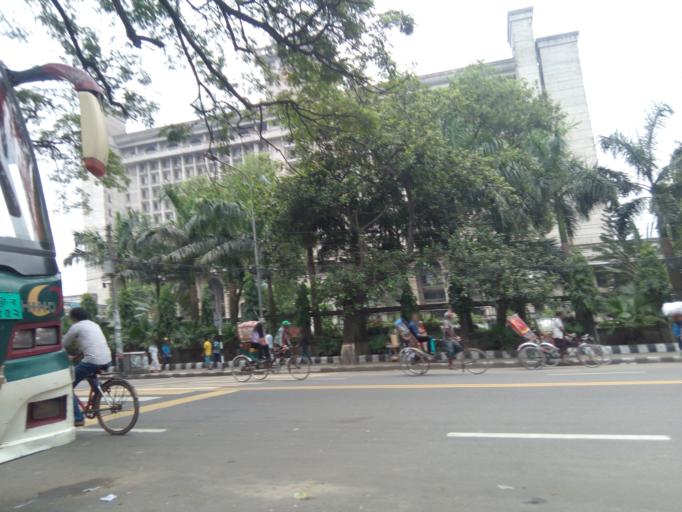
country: BD
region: Dhaka
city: Paltan
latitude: 23.7249
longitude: 90.4081
